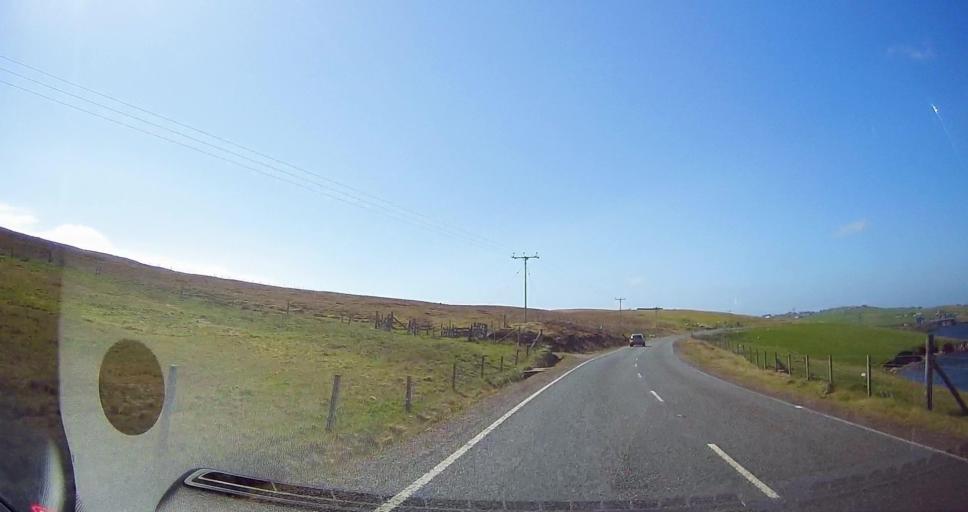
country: GB
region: Scotland
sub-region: Shetland Islands
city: Sandwick
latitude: 60.1088
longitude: -1.2970
